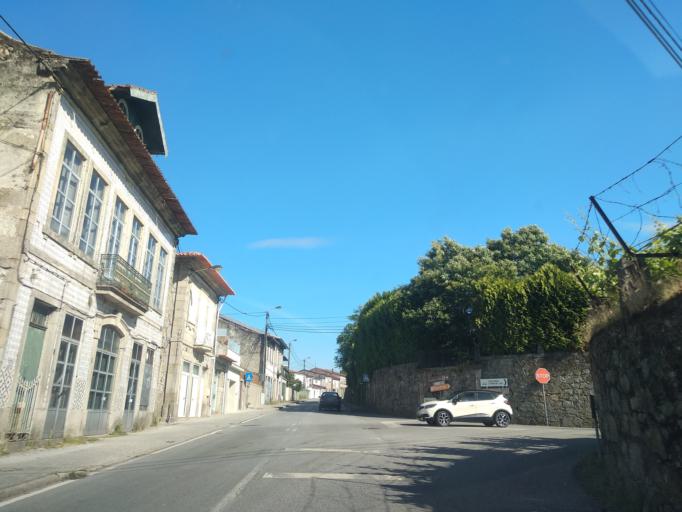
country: PT
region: Braga
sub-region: Vila Verde
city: Prado
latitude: 41.5878
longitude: -8.4573
